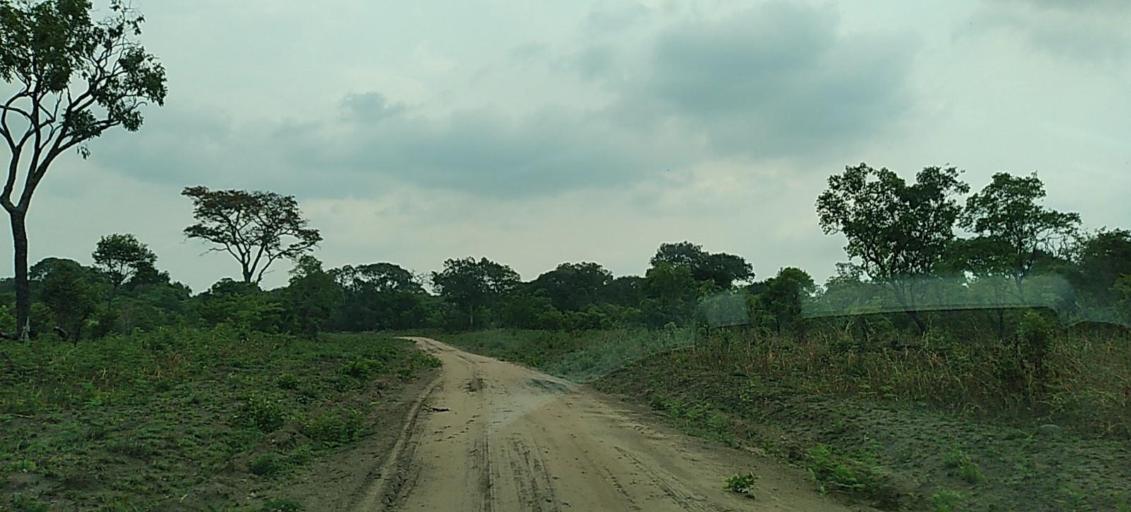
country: ZM
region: North-Western
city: Mwinilunga
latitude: -11.4076
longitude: 24.6220
